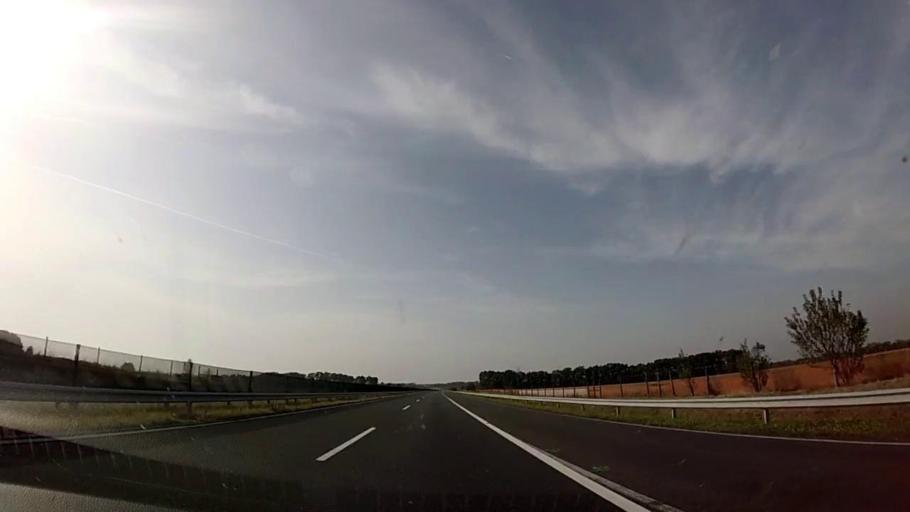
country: HU
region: Somogy
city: Balatonbereny
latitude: 46.6262
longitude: 17.2739
